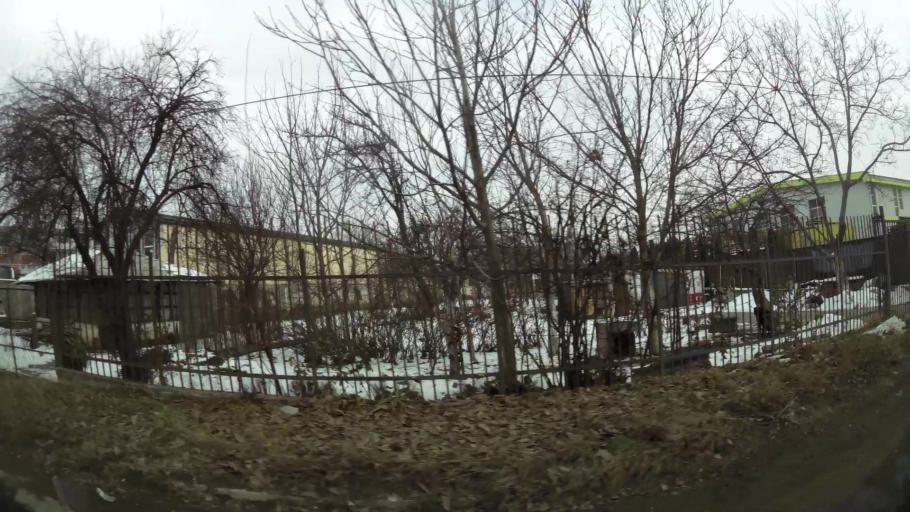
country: MK
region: Suto Orizari
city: Suto Orizare
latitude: 42.0344
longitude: 21.4009
